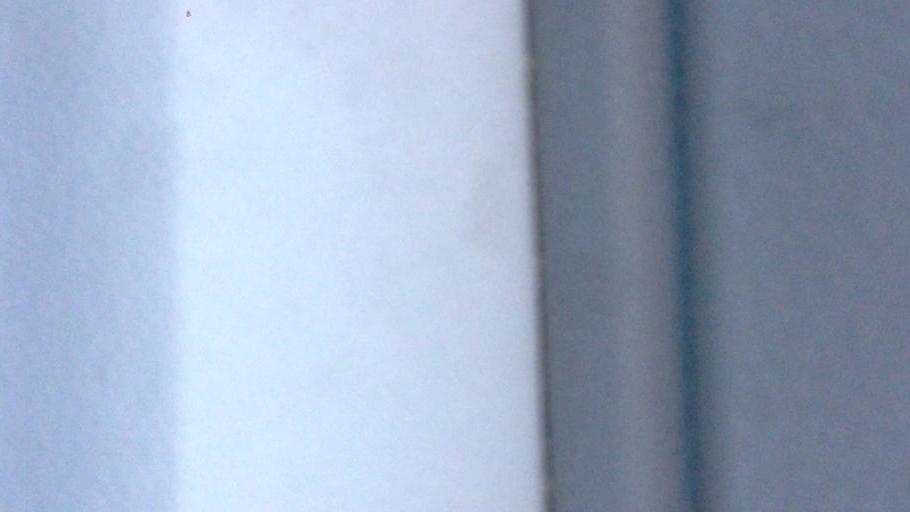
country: US
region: New York
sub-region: Ulster County
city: Lake Katrine
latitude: 41.9878
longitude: -73.9688
